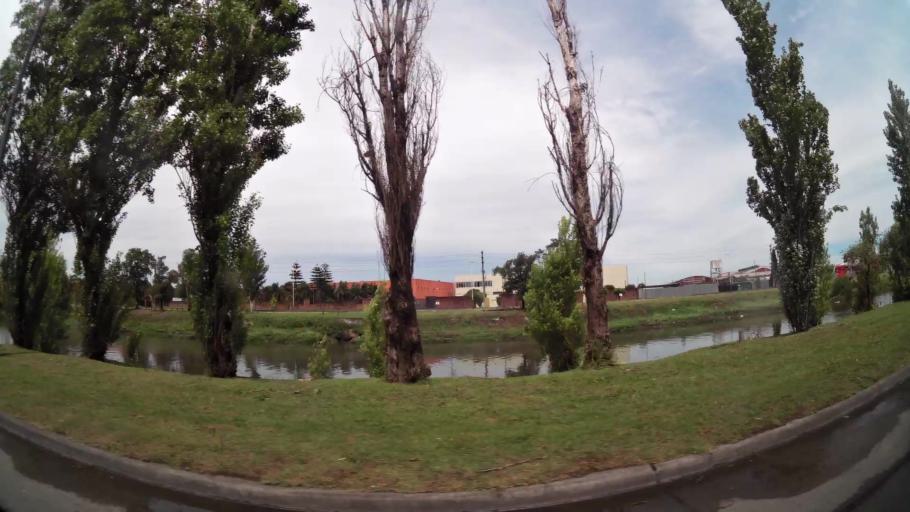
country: AR
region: Buenos Aires F.D.
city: Villa Lugano
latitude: -34.6842
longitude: -58.4437
